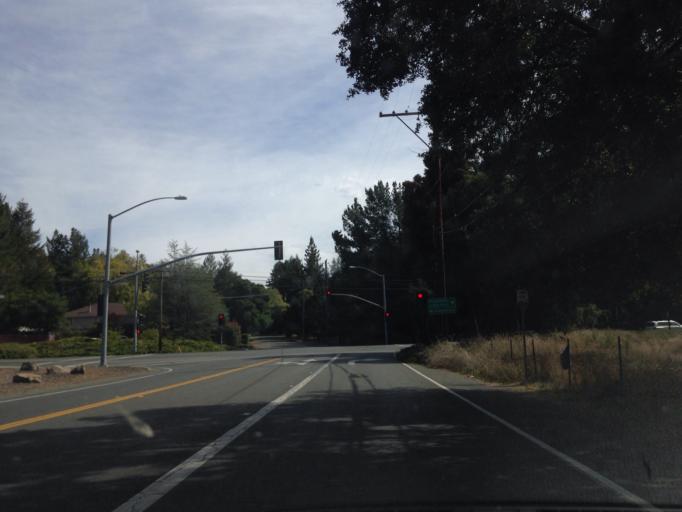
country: US
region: California
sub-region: Sonoma County
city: Graton
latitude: 38.4369
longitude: -122.8584
